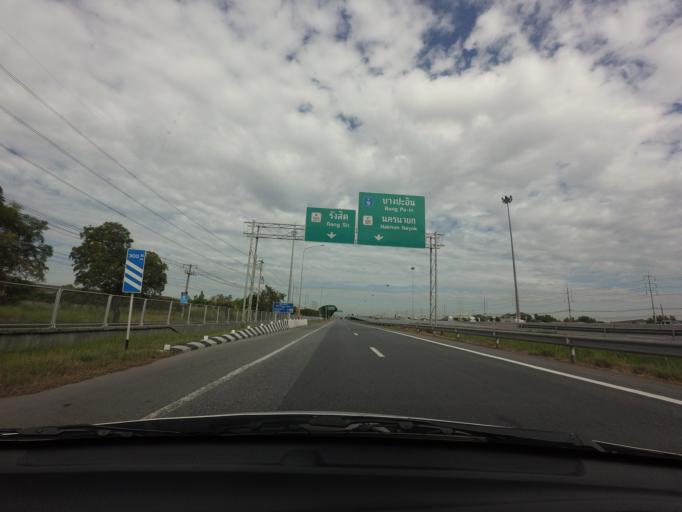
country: TH
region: Pathum Thani
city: Thanyaburi
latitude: 13.9974
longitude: 100.7092
